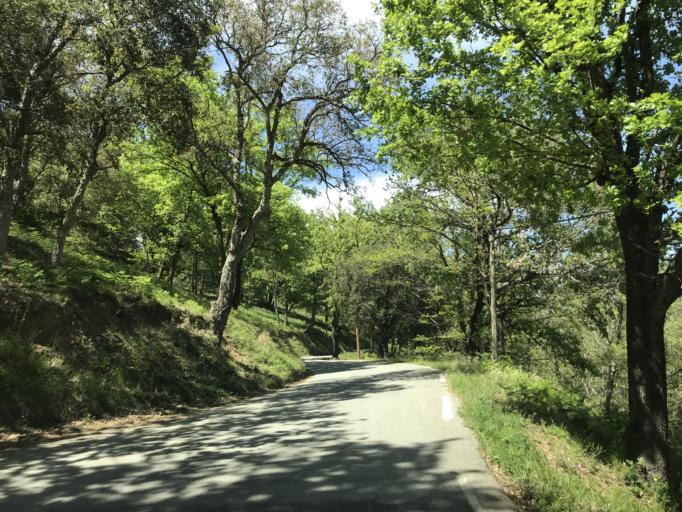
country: FR
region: Provence-Alpes-Cote d'Azur
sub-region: Departement du Var
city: Tanneron
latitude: 43.5827
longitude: 6.8236
